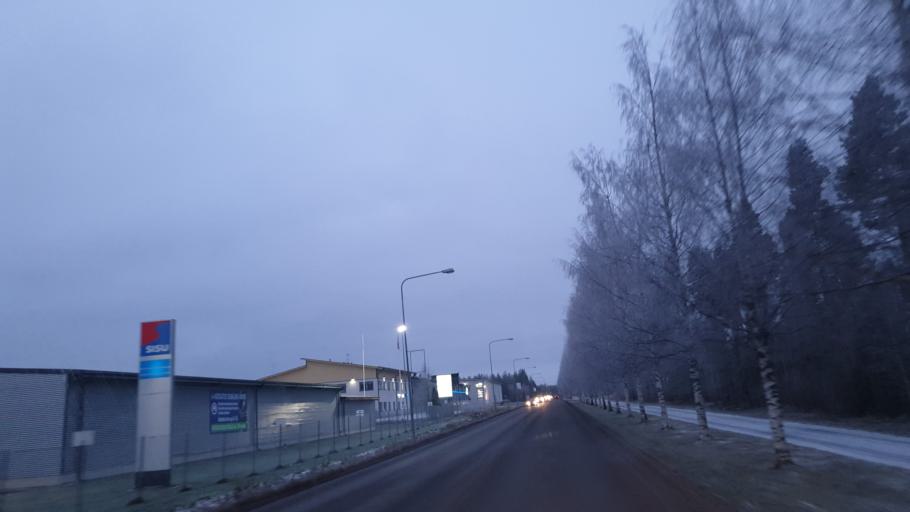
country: FI
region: Southern Ostrobothnia
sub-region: Seinaejoki
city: Nurmo
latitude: 62.7843
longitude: 22.9008
